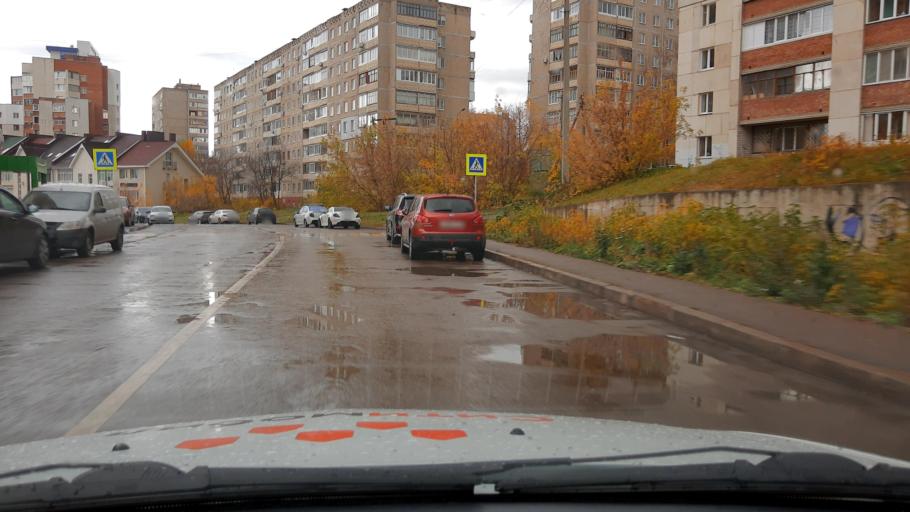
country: RU
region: Bashkortostan
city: Ufa
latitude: 54.6924
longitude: 55.9945
